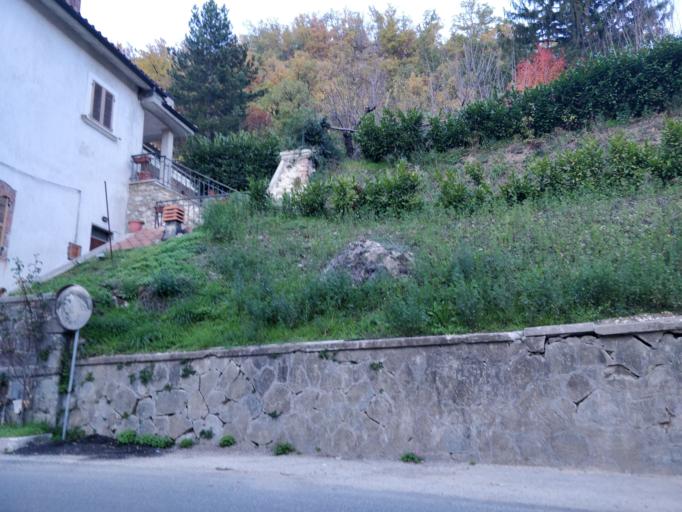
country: IT
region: The Marches
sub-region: Provincia di Ascoli Piceno
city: Arquata del Tronto
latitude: 42.7752
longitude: 13.2959
